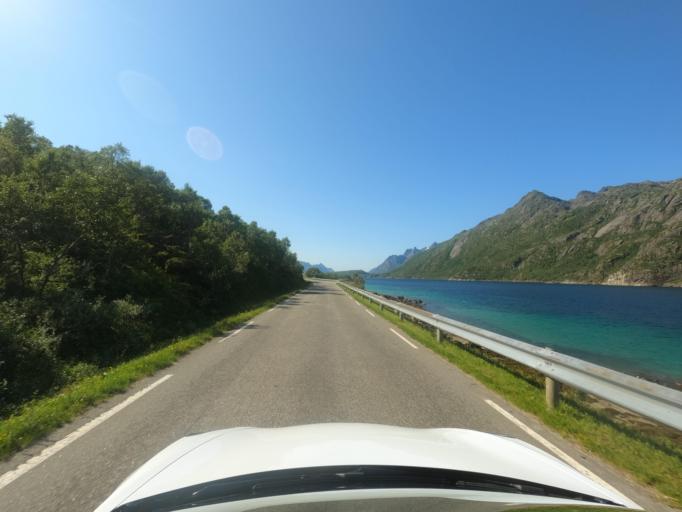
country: NO
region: Nordland
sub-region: Hadsel
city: Stokmarknes
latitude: 68.3895
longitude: 15.0993
